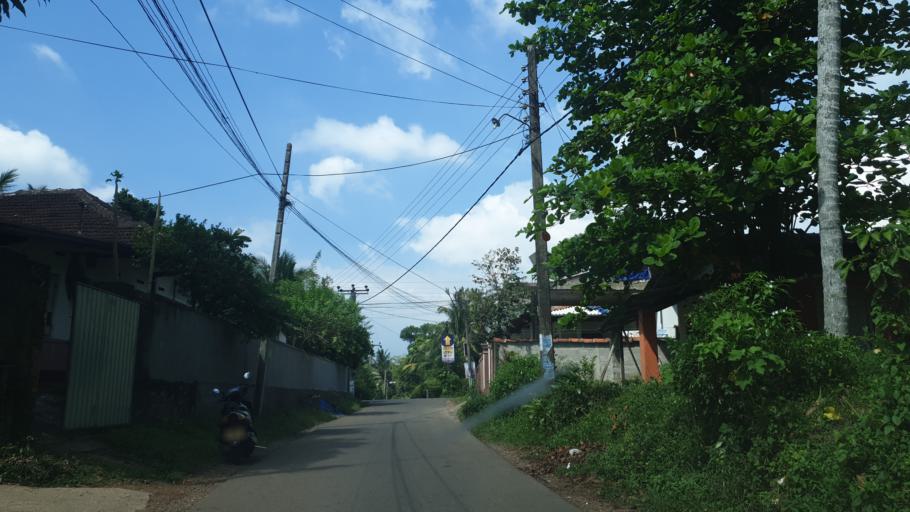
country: LK
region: Western
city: Horana South
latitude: 6.7052
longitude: 79.9847
